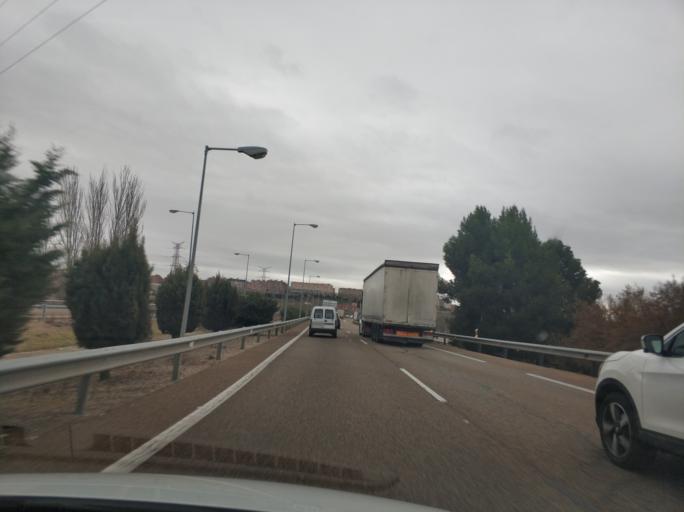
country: ES
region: Castille and Leon
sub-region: Provincia de Valladolid
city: Zaratan
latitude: 41.6520
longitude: -4.7652
